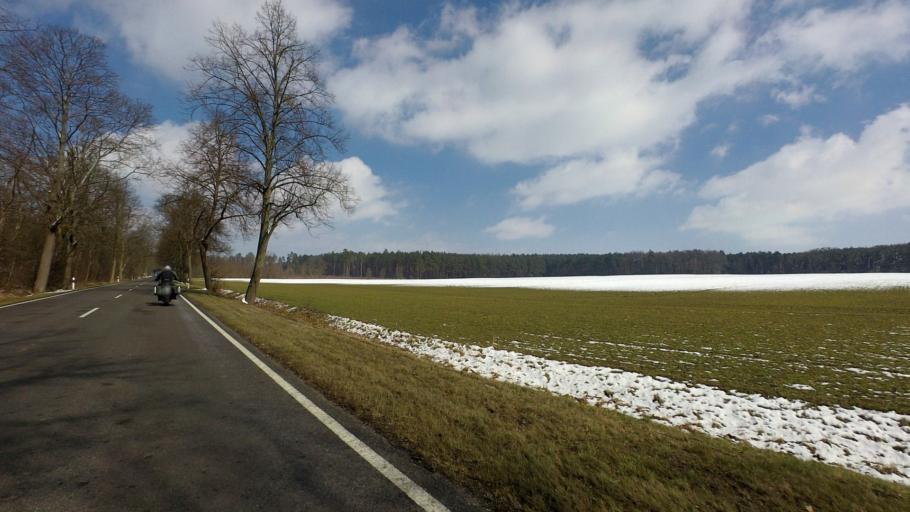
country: DE
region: Brandenburg
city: Werftpfuhl
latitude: 52.7133
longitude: 13.8370
